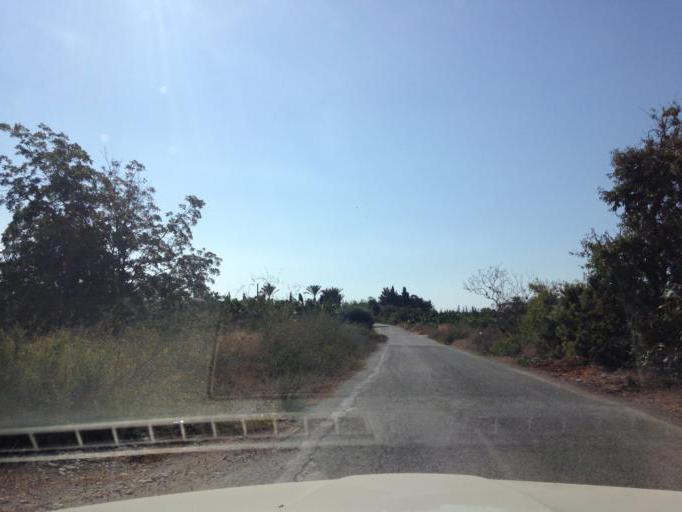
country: CY
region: Pafos
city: Pegeia
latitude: 34.8641
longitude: 32.3628
